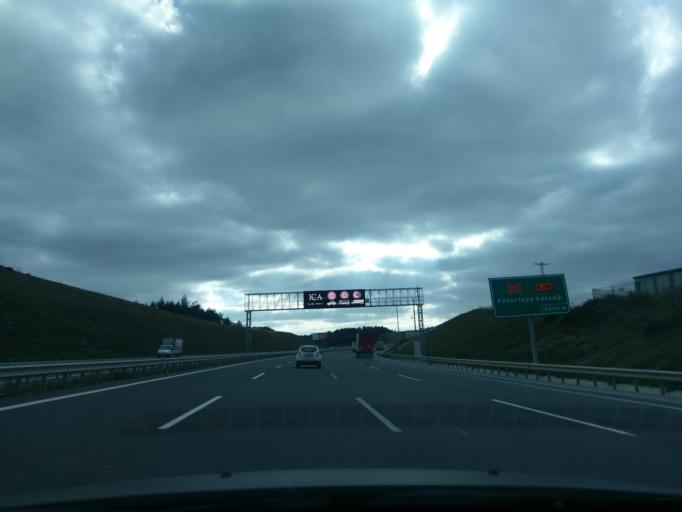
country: TR
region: Istanbul
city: Basaksehir
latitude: 41.1596
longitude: 28.8104
